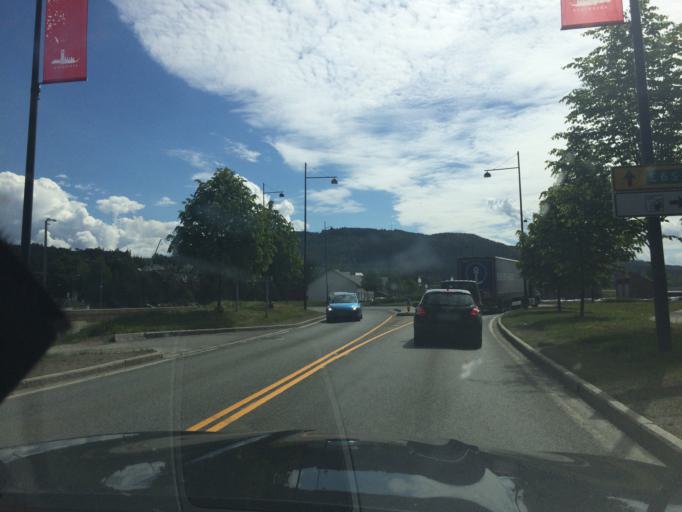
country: NO
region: Nord-Trondelag
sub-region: Steinkjer
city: Steinkjer
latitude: 64.0113
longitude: 11.4950
